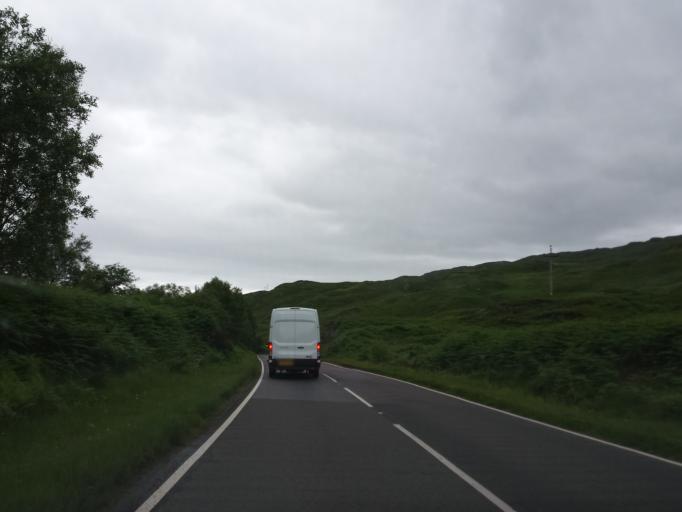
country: GB
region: Scotland
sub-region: Argyll and Bute
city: Isle Of Mull
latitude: 56.8851
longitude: -5.6174
